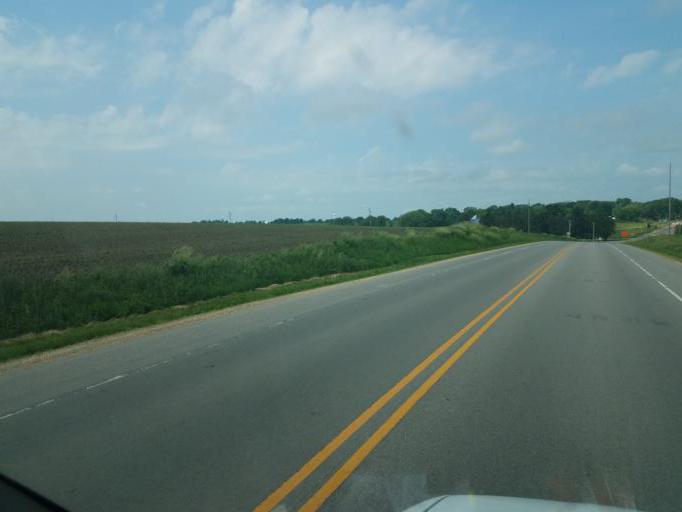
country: US
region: Wisconsin
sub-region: Monroe County
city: Cashton
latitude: 43.7402
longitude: -90.7672
